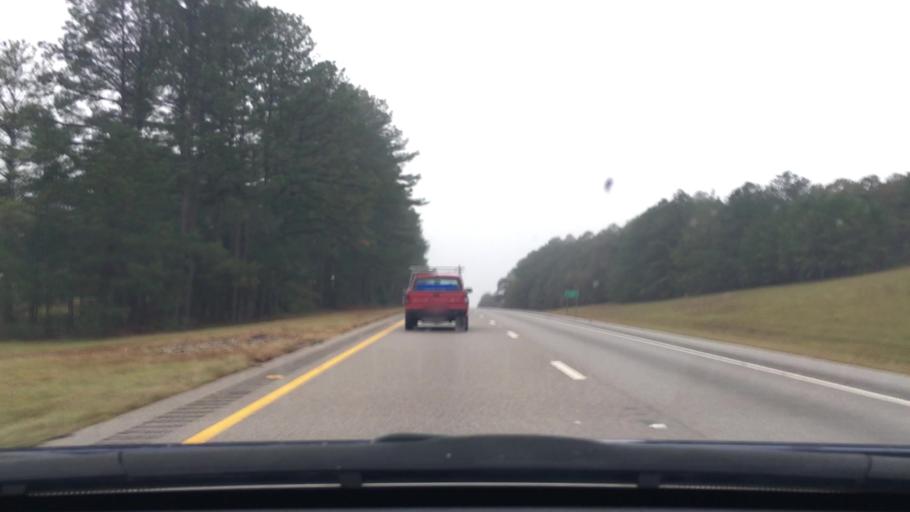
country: US
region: South Carolina
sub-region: Kershaw County
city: Camden
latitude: 34.2088
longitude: -80.4619
